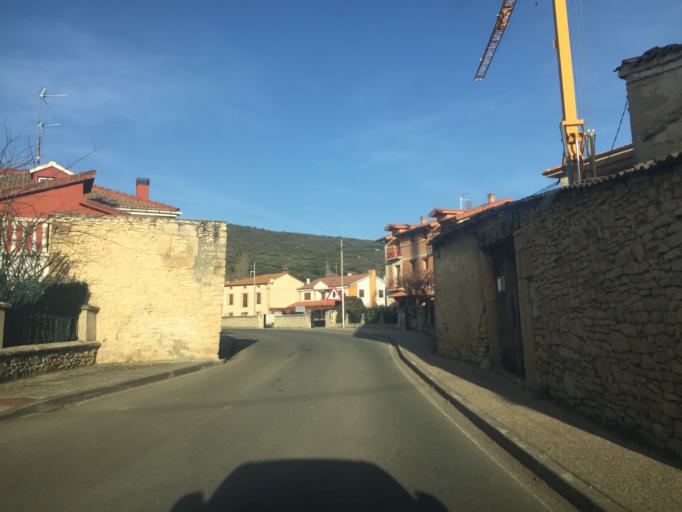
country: ES
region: Castille and Leon
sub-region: Provincia de Burgos
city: Medina de Pomar
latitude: 42.9413
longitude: -3.5981
